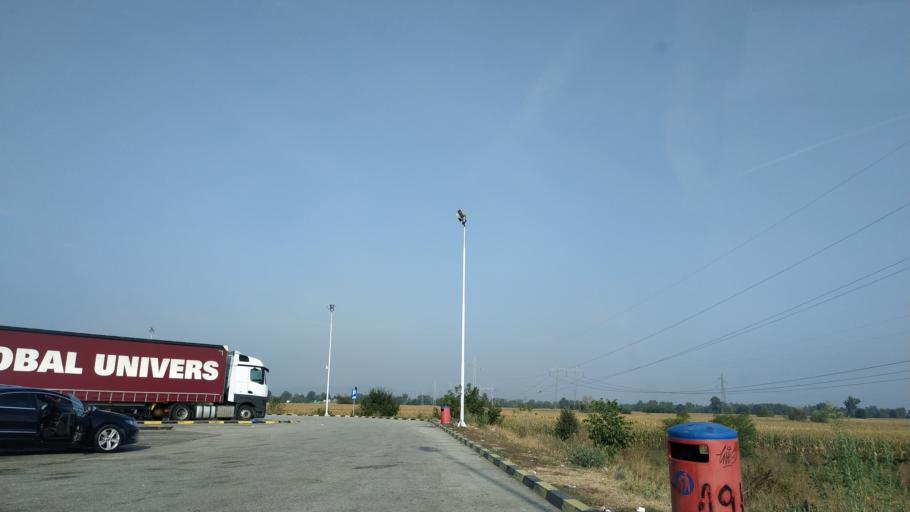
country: RS
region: Central Serbia
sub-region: Pomoravski Okrug
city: Cuprija
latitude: 43.9552
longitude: 21.3641
